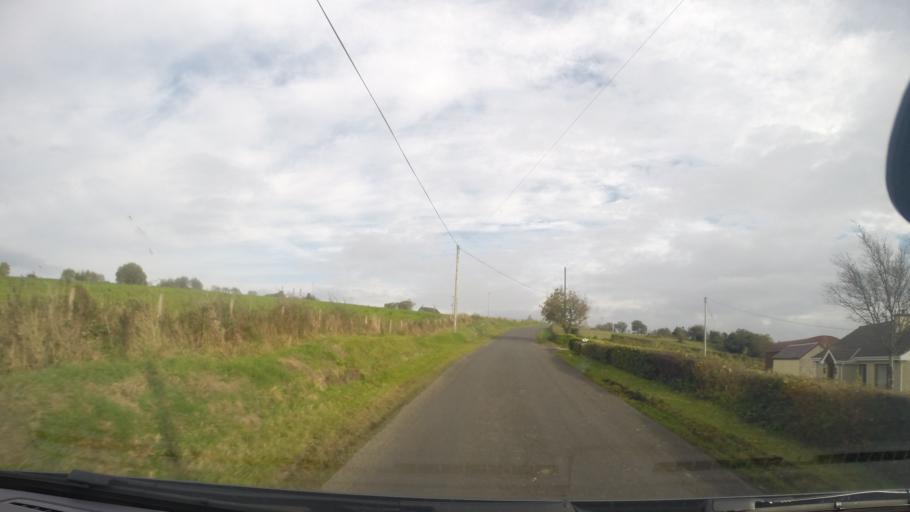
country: IE
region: Ulster
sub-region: County Donegal
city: Ballyshannon
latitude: 54.4180
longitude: -8.0415
